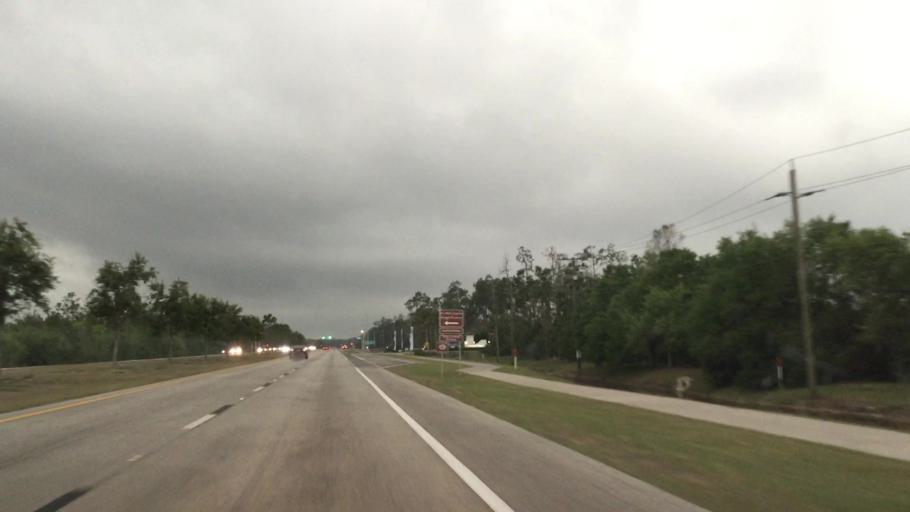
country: US
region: Florida
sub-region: Lee County
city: Villas
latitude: 26.5747
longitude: -81.8263
